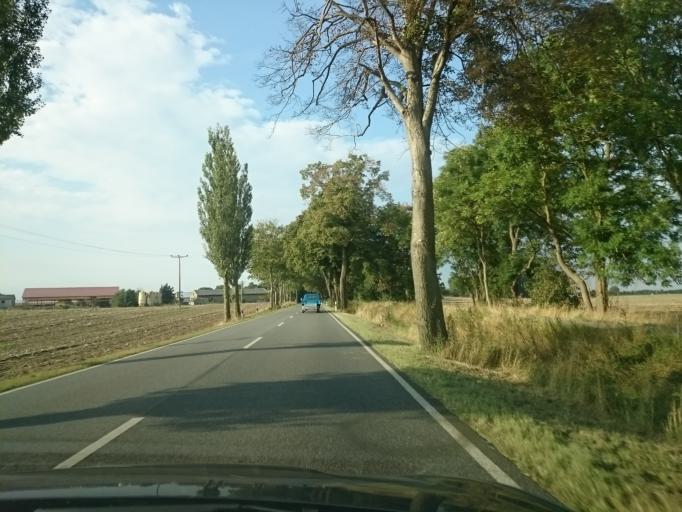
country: DE
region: Mecklenburg-Vorpommern
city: Borrentin
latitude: 53.8549
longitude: 13.0032
